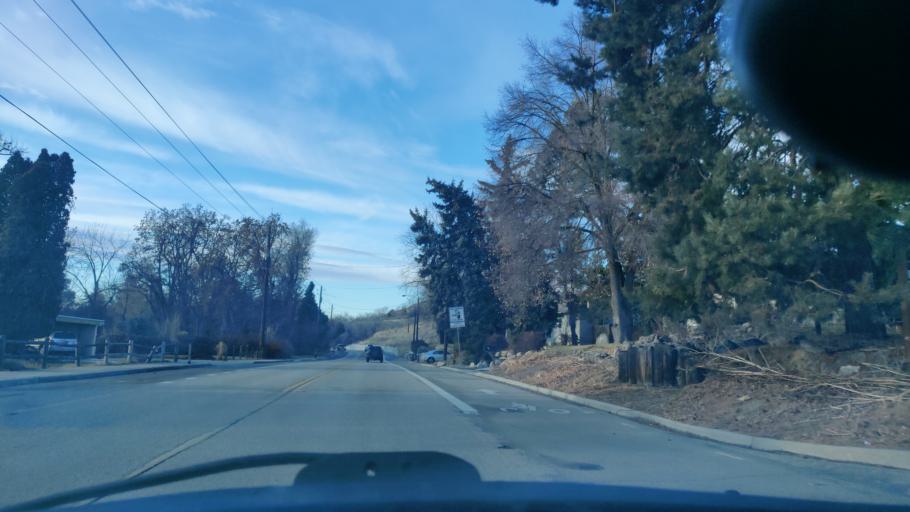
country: US
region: Idaho
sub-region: Ada County
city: Garden City
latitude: 43.6500
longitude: -116.2249
